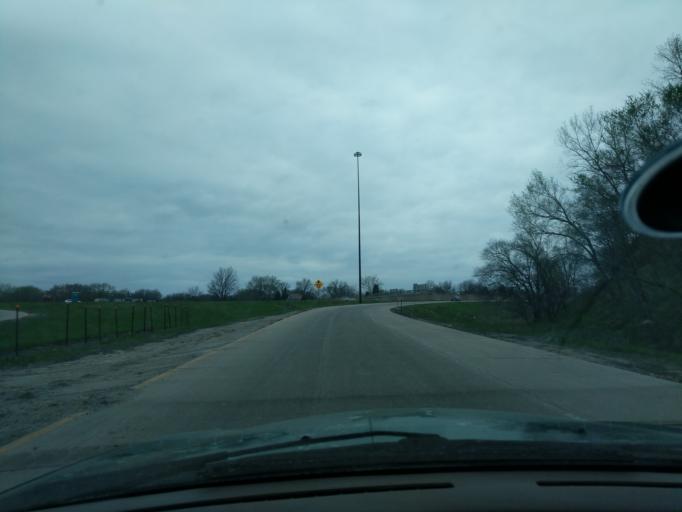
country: US
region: Nebraska
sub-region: Douglas County
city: Ralston
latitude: 41.2355
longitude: -96.0843
